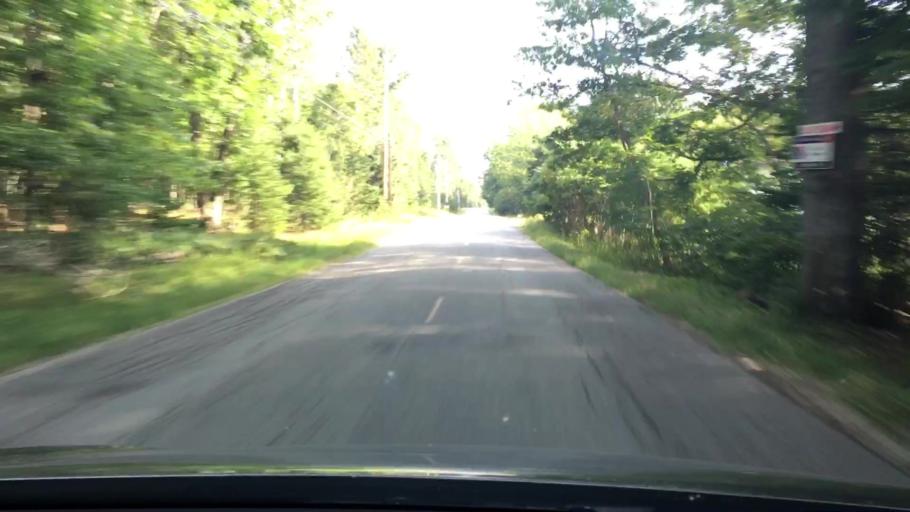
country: US
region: Maine
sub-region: Hancock County
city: Bucksport
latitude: 44.5388
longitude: -68.7948
